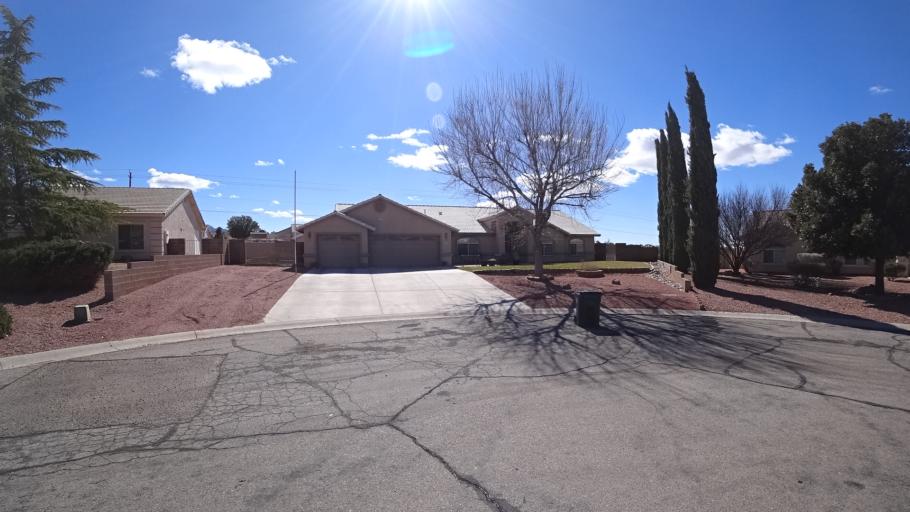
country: US
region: Arizona
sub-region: Mohave County
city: Kingman
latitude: 35.2030
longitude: -113.9754
